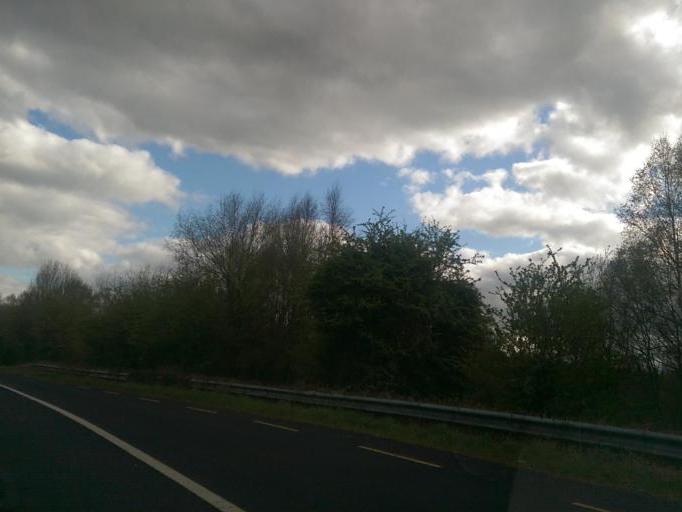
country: IE
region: Connaught
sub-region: County Galway
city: Ballinasloe
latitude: 53.3496
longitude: -8.2530
